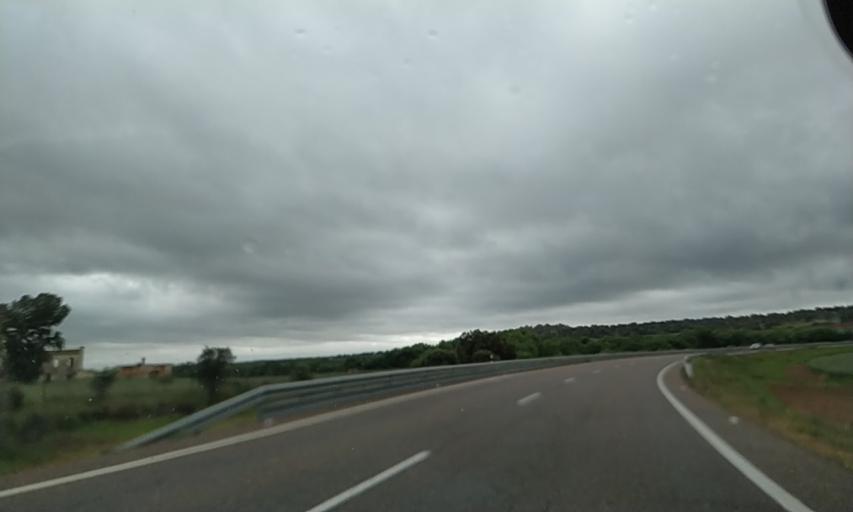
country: ES
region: Extremadura
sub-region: Provincia de Badajoz
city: La Roca de la Sierra
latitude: 39.0582
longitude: -6.7715
